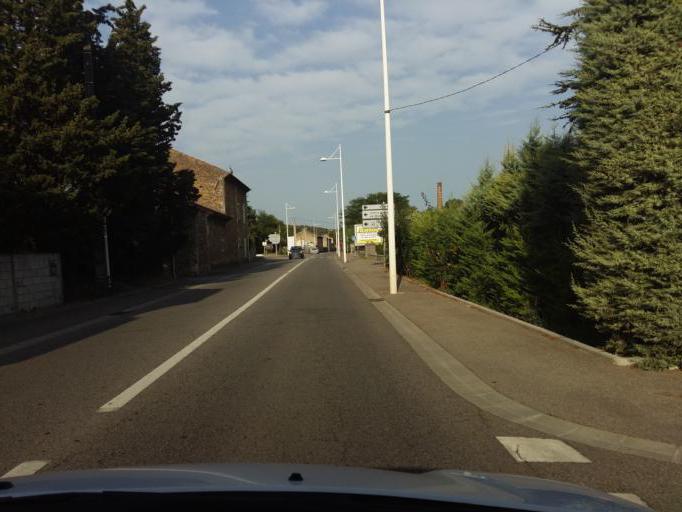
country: FR
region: Provence-Alpes-Cote d'Azur
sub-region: Departement du Vaucluse
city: Bollene
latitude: 44.2785
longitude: 4.7753
